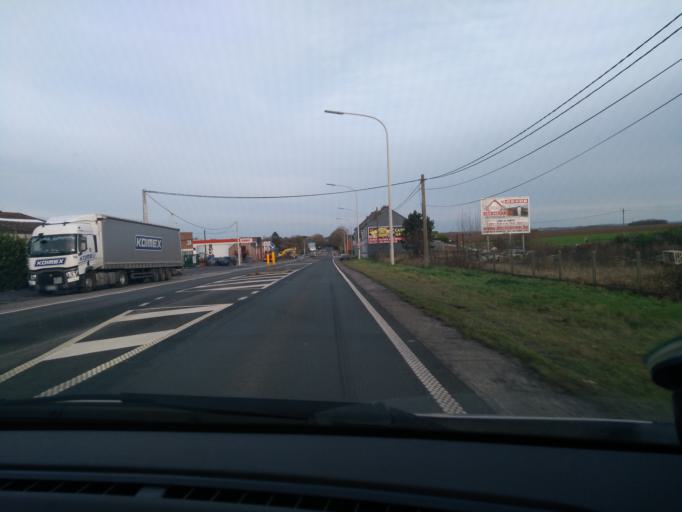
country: BE
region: Wallonia
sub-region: Province du Hainaut
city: Quevy-le-Petit
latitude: 50.3643
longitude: 3.9674
